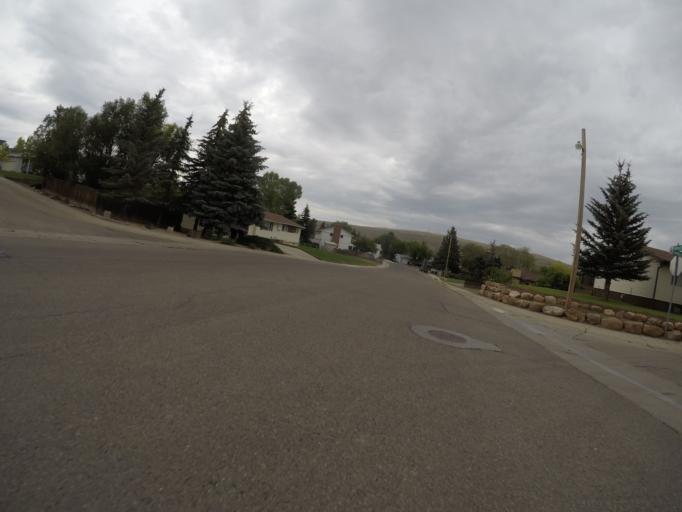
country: US
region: Wyoming
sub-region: Lincoln County
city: Kemmerer
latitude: 41.7906
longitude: -110.5455
